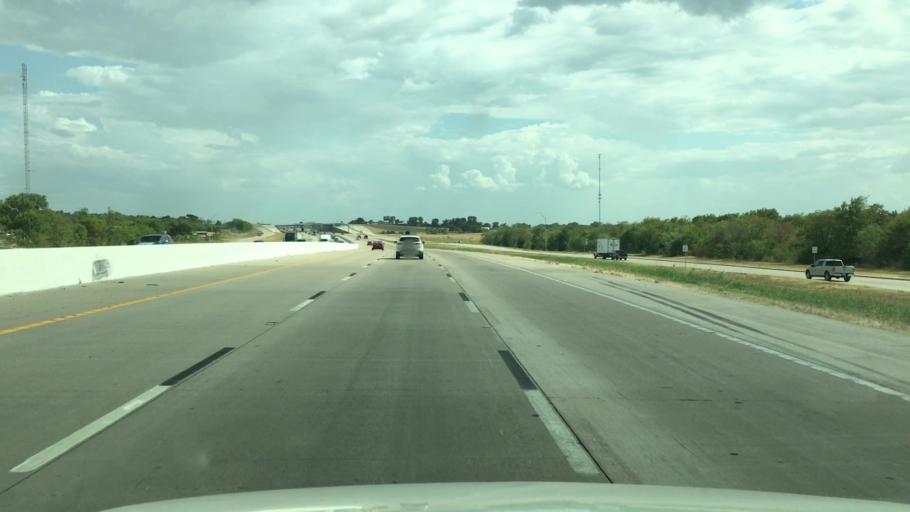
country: US
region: Texas
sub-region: McLennan County
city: West
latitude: 31.7971
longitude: -97.1023
